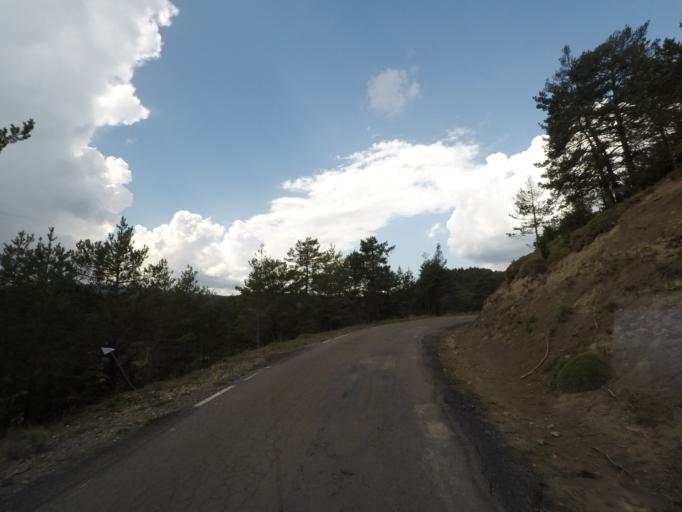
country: ES
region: Aragon
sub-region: Provincia de Huesca
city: Fiscal
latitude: 42.4039
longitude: -0.0814
